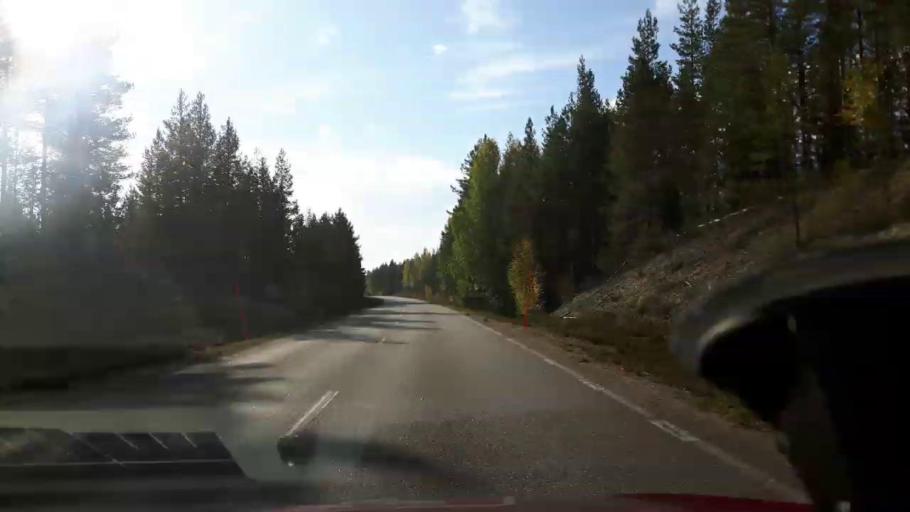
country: SE
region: Vaesternorrland
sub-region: Ange Kommun
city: Ange
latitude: 62.0720
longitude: 15.1028
